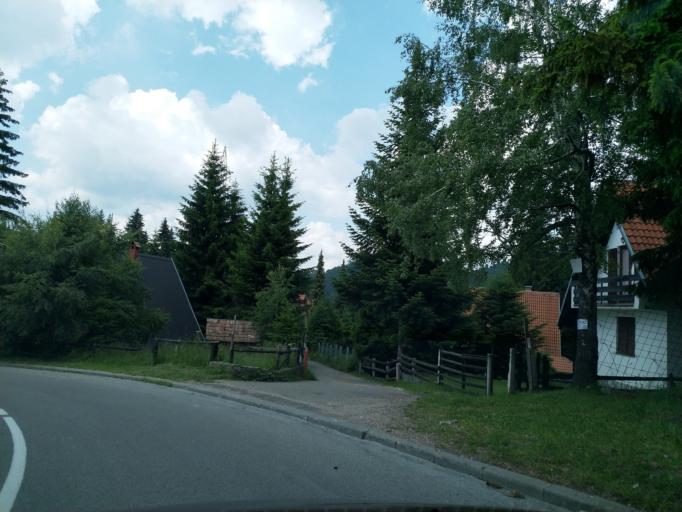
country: RS
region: Central Serbia
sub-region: Raski Okrug
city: Raska
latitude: 43.2744
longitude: 20.7811
